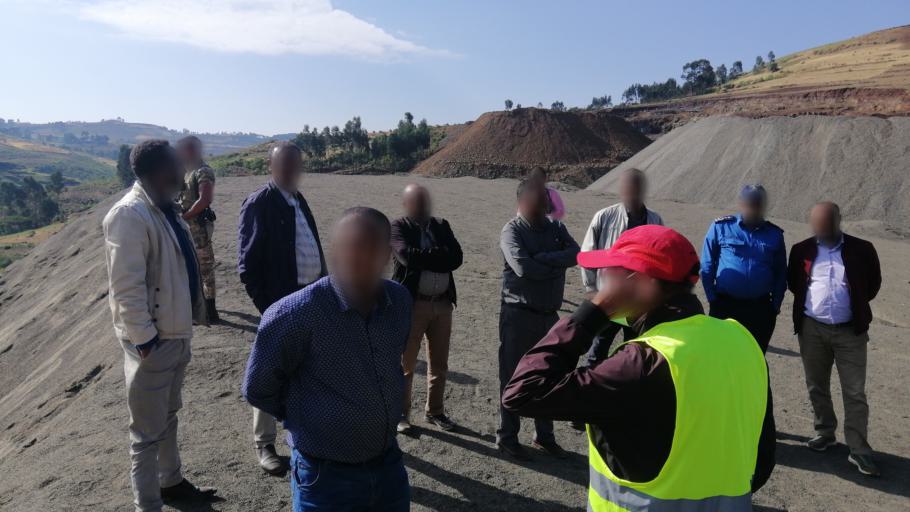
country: ET
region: Amhara
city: Debre Tabor
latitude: 11.5562
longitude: 38.1438
